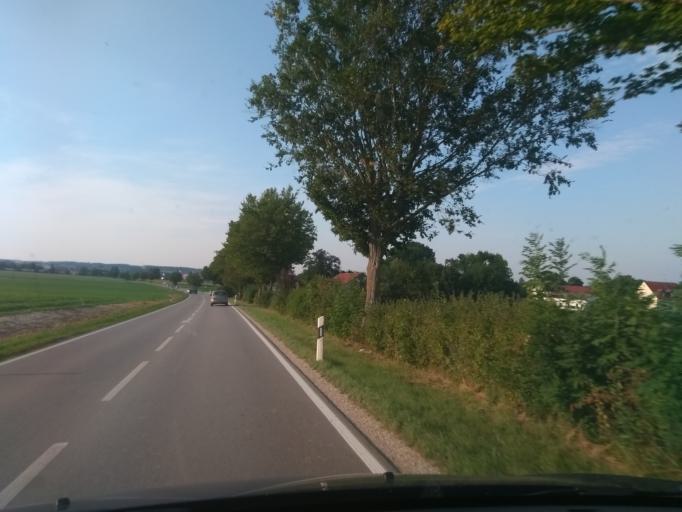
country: DE
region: Bavaria
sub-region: Upper Bavaria
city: Markt Indersdorf
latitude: 48.3398
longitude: 11.3885
